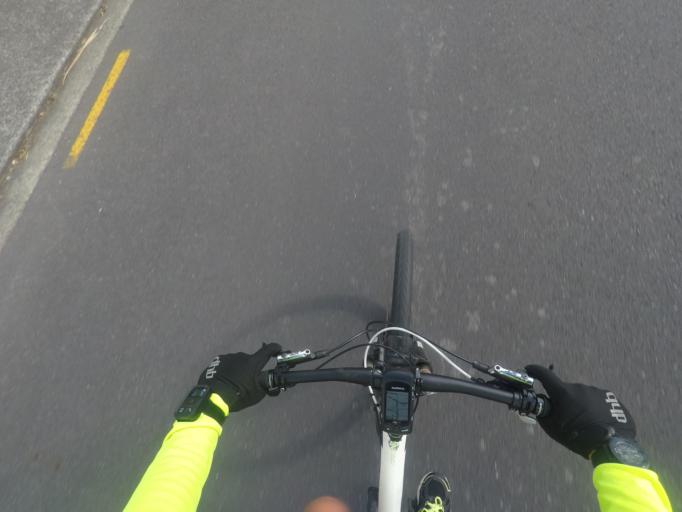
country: NZ
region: Auckland
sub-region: Auckland
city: Auckland
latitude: -36.8913
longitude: 174.7703
